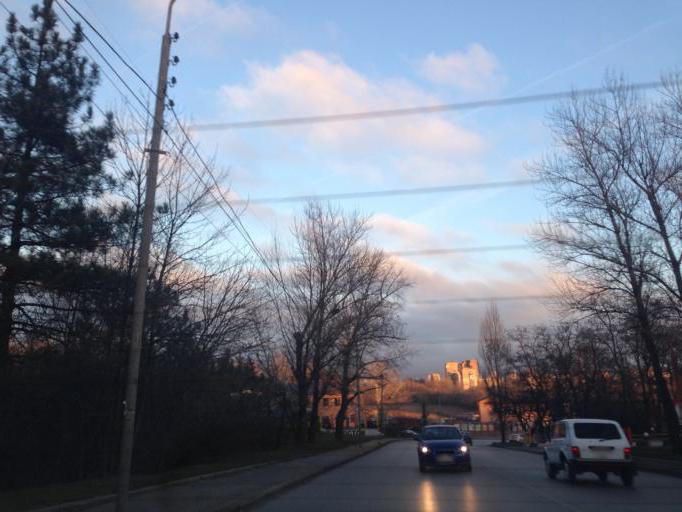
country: RU
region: Rostov
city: Rostov-na-Donu
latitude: 47.2474
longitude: 39.6568
